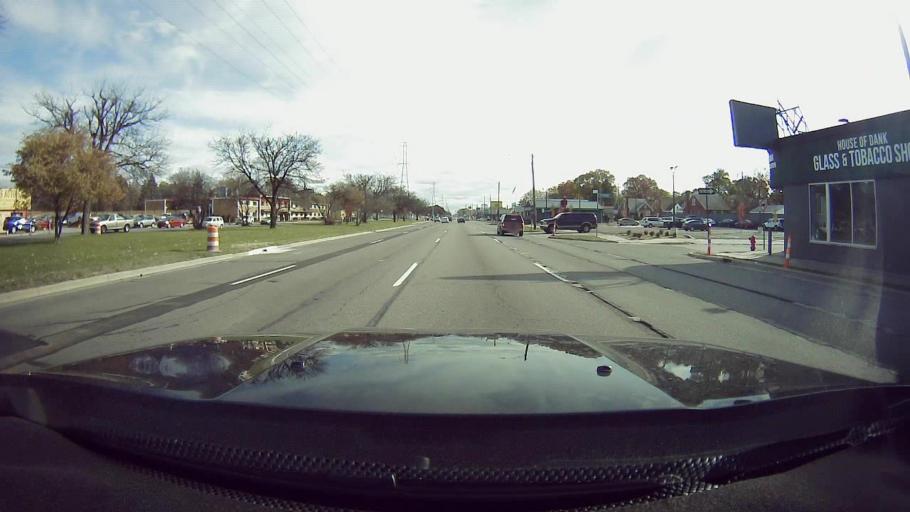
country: US
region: Michigan
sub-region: Oakland County
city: Hazel Park
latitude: 42.4472
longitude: -83.0713
